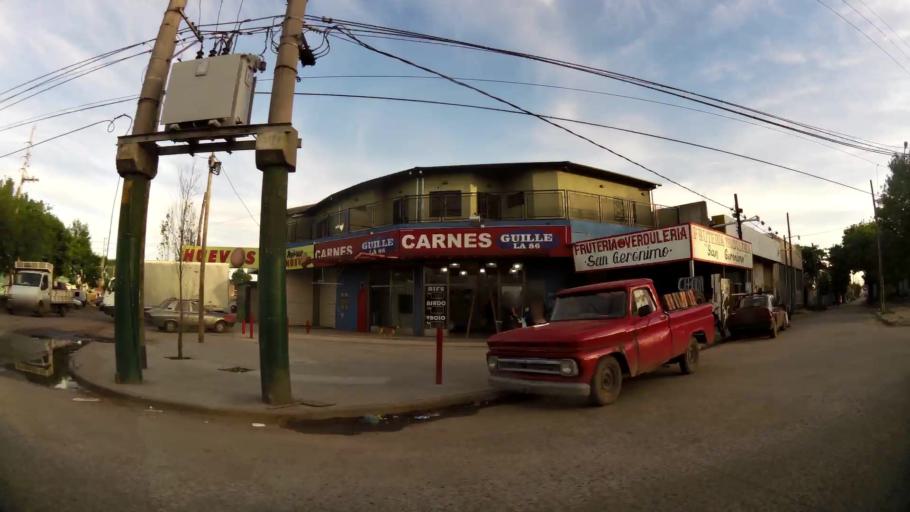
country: AR
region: Buenos Aires
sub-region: Partido de Almirante Brown
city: Adrogue
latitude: -34.7846
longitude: -58.3443
